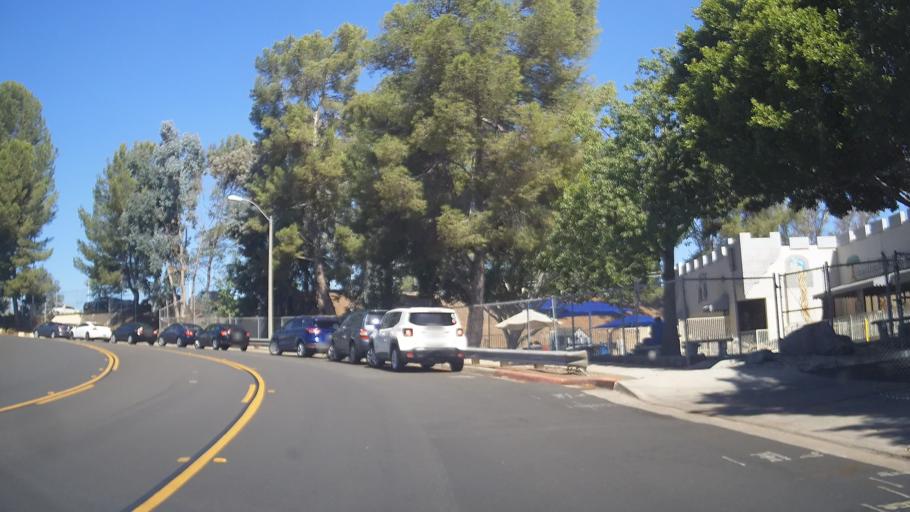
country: US
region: California
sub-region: San Diego County
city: La Mesa
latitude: 32.8281
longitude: -117.1216
